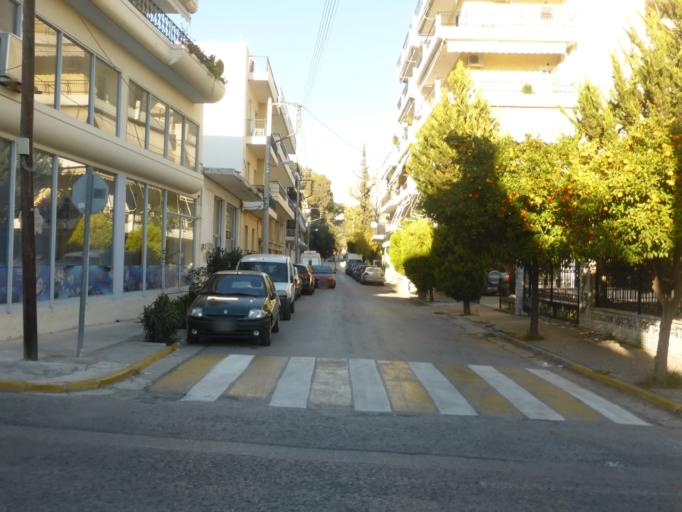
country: GR
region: Attica
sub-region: Nomarchia Athinas
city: Peristeri
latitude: 38.0146
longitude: 23.6864
